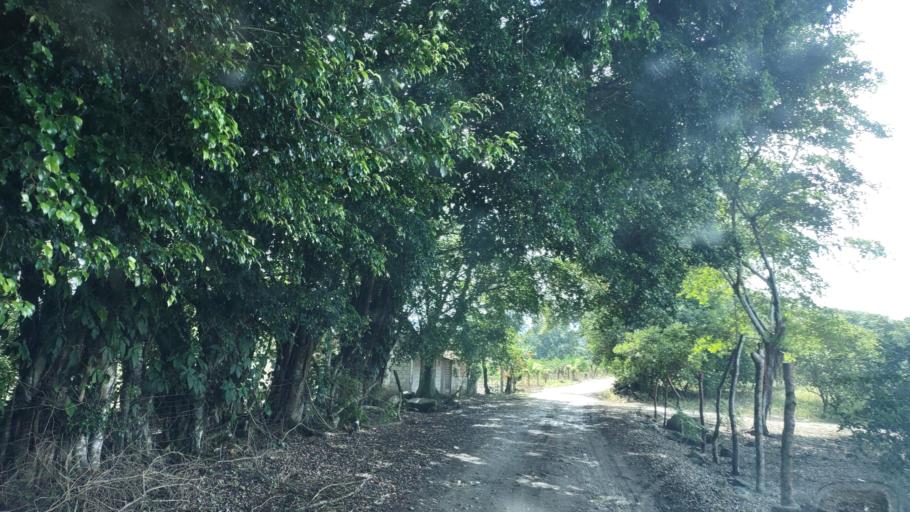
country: MX
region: Veracruz
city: Santa Cruz Hidalgo
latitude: 19.9952
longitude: -96.9601
